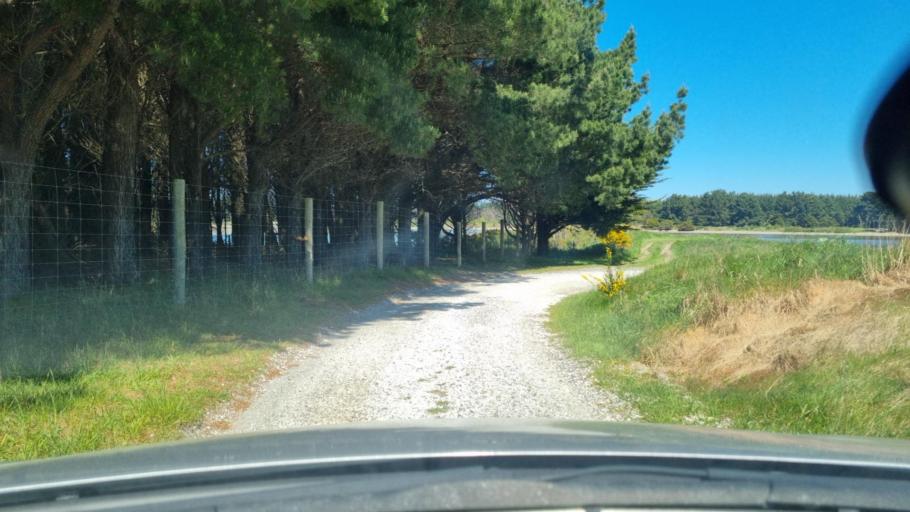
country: NZ
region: Southland
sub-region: Invercargill City
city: Invercargill
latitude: -46.4585
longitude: 168.2702
